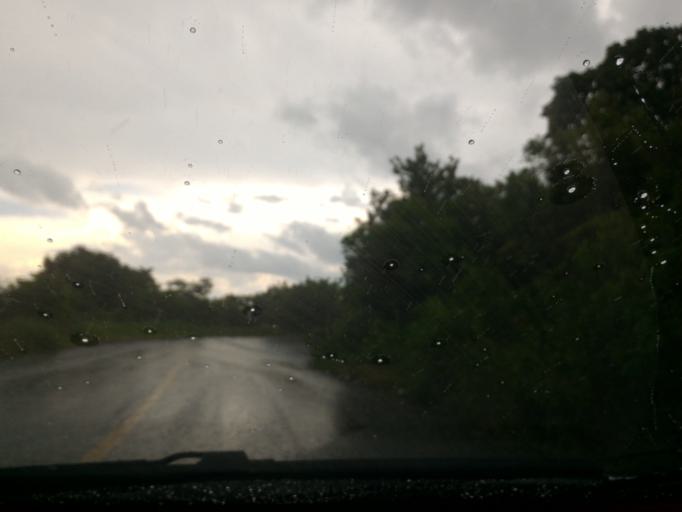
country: MX
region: Jalisco
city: San Andres Ixtlan
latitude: 19.8343
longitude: -103.4616
